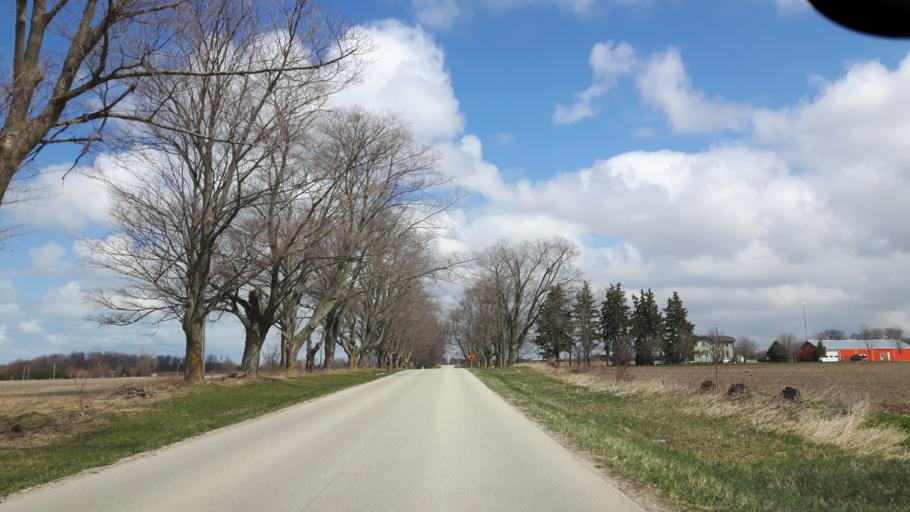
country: CA
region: Ontario
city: Goderich
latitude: 43.6385
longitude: -81.6846
